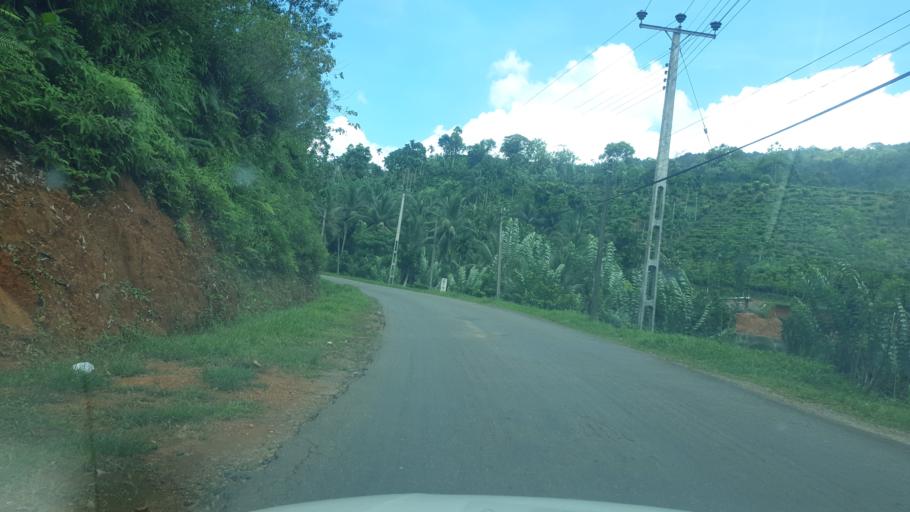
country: LK
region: Sabaragamuwa
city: Ratnapura
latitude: 6.4887
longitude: 80.4006
